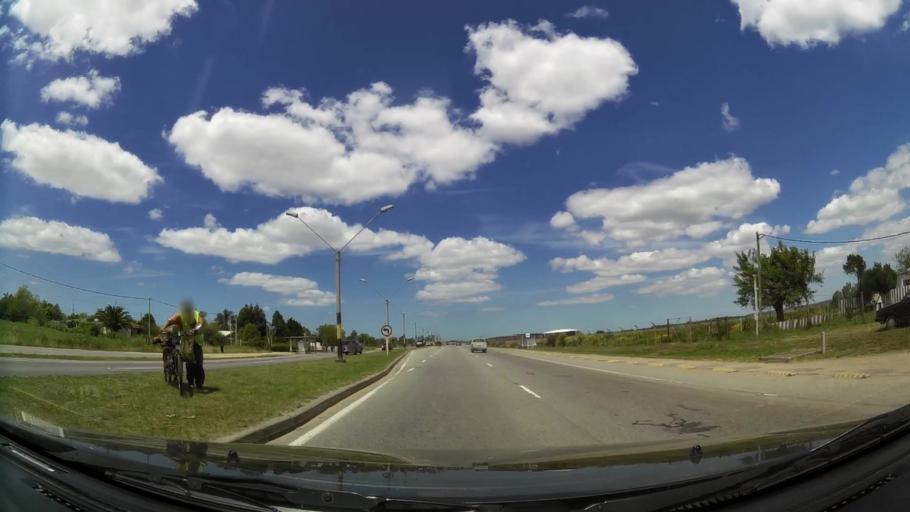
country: UY
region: Canelones
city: Colonia Nicolich
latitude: -34.8235
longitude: -56.0093
